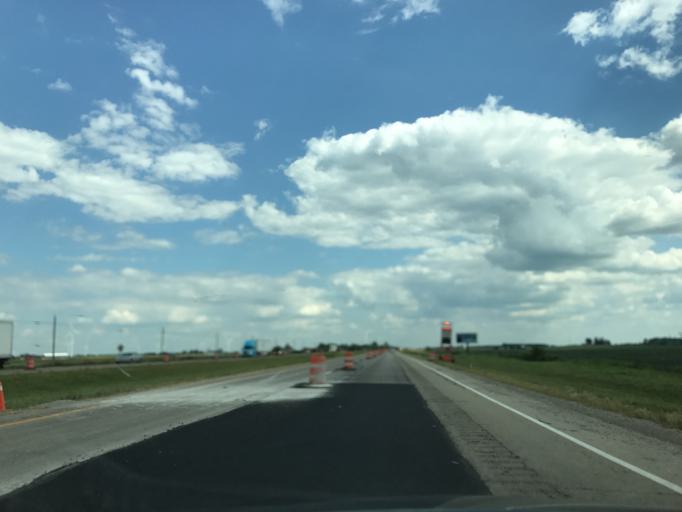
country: US
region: Ohio
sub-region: Van Wert County
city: Convoy
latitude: 40.9517
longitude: -84.7243
